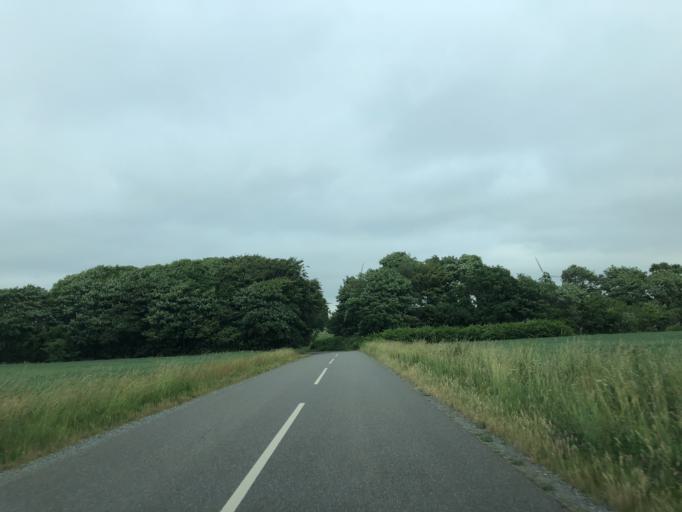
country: DK
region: Central Jutland
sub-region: Holstebro Kommune
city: Holstebro
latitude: 56.2405
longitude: 8.6170
